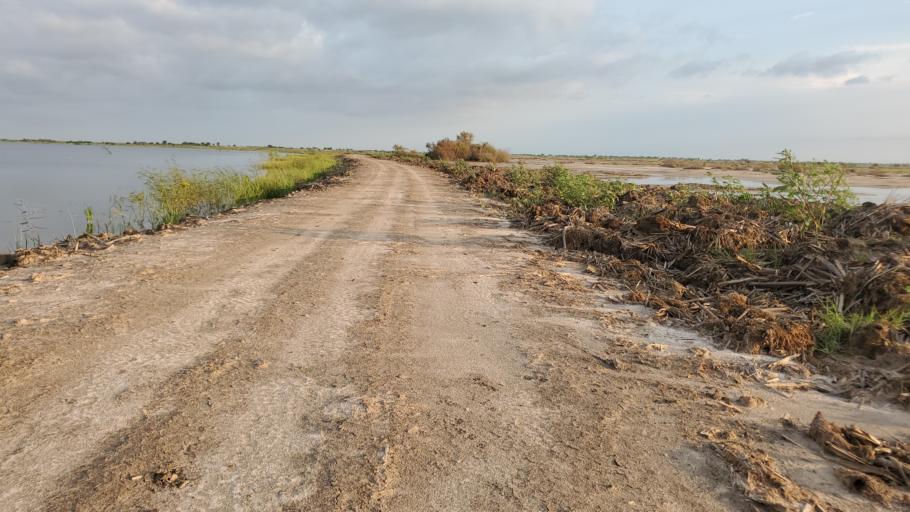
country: SN
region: Saint-Louis
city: Saint-Louis
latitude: 16.0253
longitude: -16.4102
